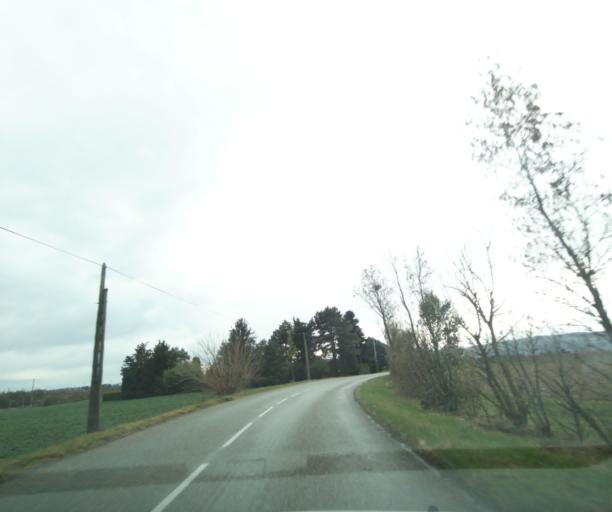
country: FR
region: Rhone-Alpes
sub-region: Departement de la Drome
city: Bourg-les-Valence
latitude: 44.9635
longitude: 4.9313
